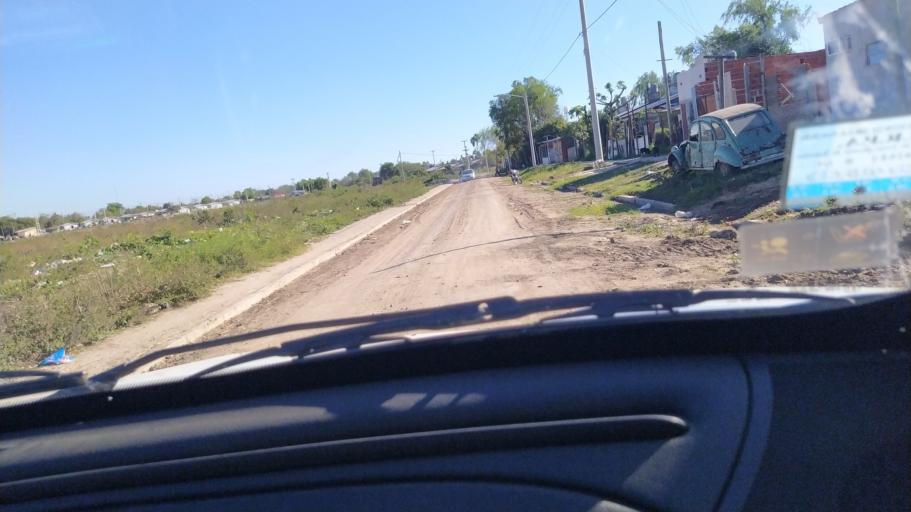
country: AR
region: Corrientes
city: Corrientes
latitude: -27.4985
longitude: -58.8008
